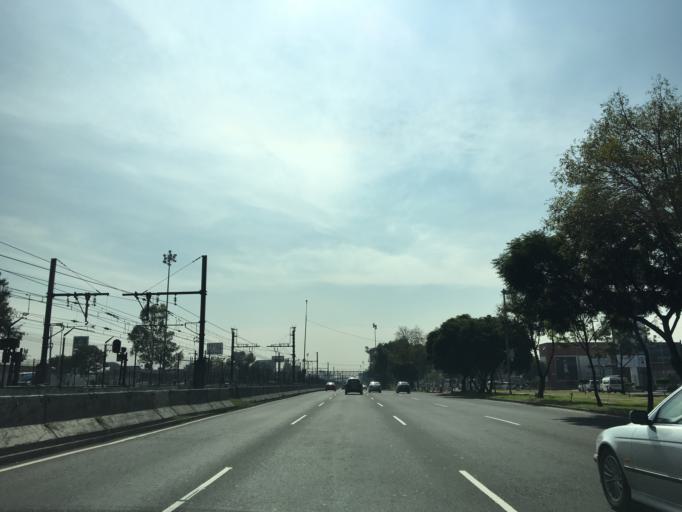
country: MX
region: Mexico City
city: Iztapalapa
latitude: 19.3967
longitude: -99.0562
